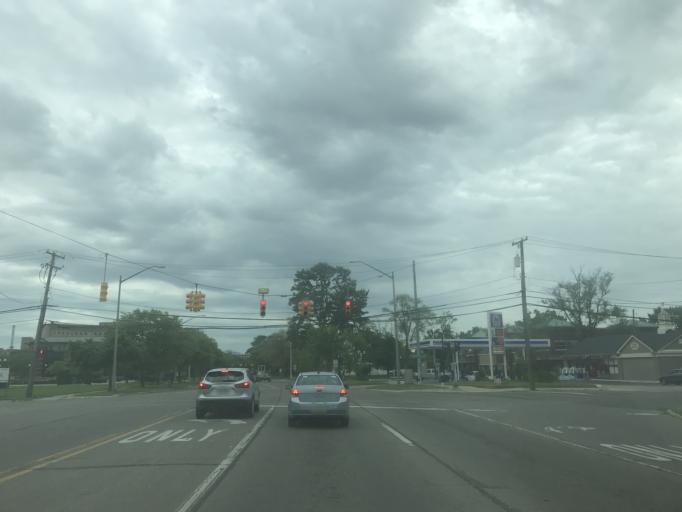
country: US
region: Michigan
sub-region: Wayne County
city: Wyandotte
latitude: 42.2146
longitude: -83.1501
